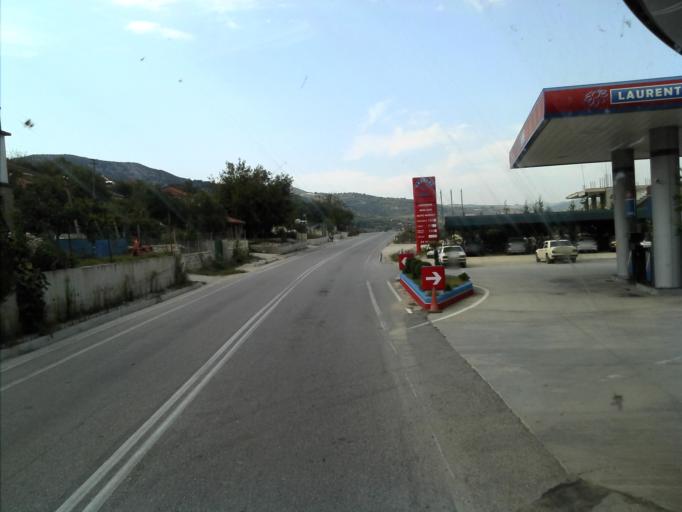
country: AL
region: Gjirokaster
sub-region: Rrethi i Tepelenes
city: Krahes
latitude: 40.4323
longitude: 19.8521
